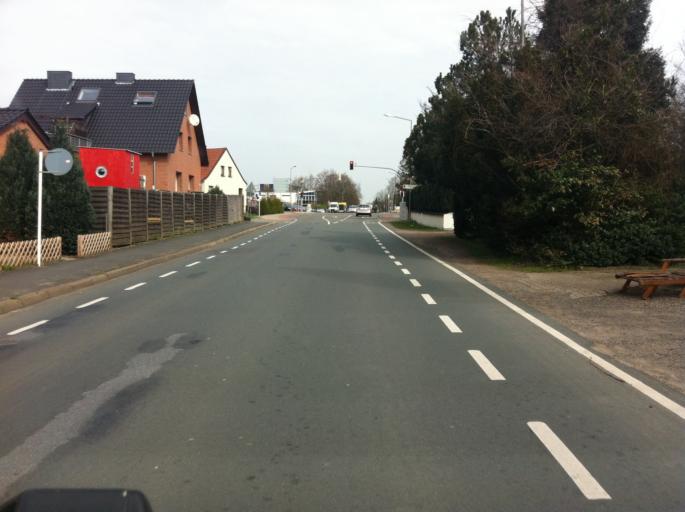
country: DE
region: North Rhine-Westphalia
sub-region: Regierungsbezirk Detmold
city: Minden
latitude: 52.2916
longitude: 8.8796
